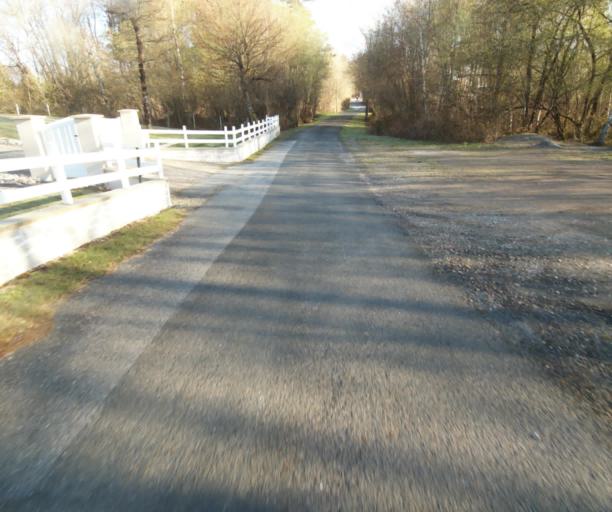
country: FR
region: Limousin
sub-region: Departement de la Correze
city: Correze
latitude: 45.3324
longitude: 1.8888
